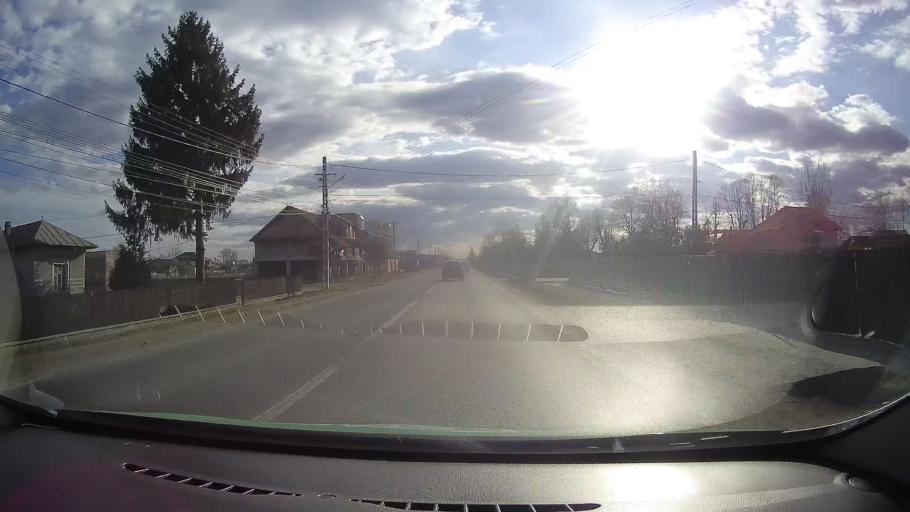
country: RO
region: Dambovita
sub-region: Comuna Lucieni
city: Lucieni
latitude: 44.8530
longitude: 25.4289
